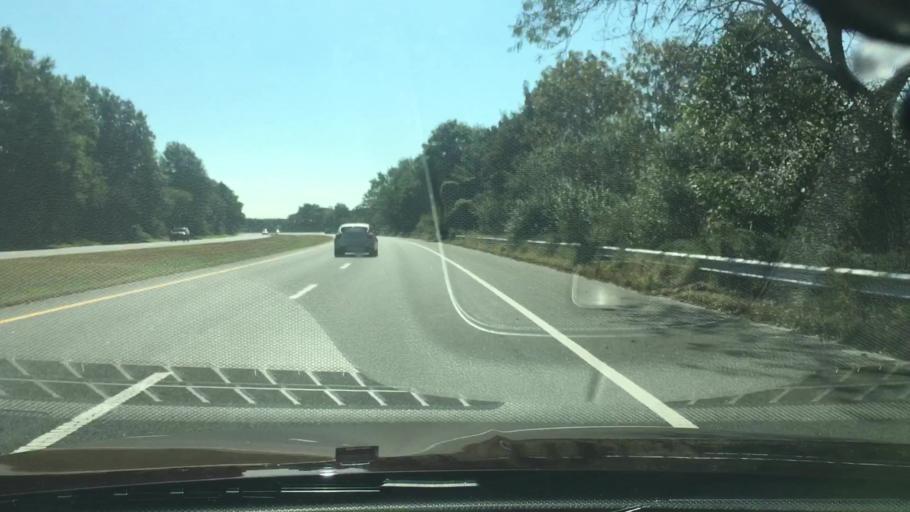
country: US
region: New York
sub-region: Suffolk County
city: North Bellport
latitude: 40.8010
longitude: -72.9593
